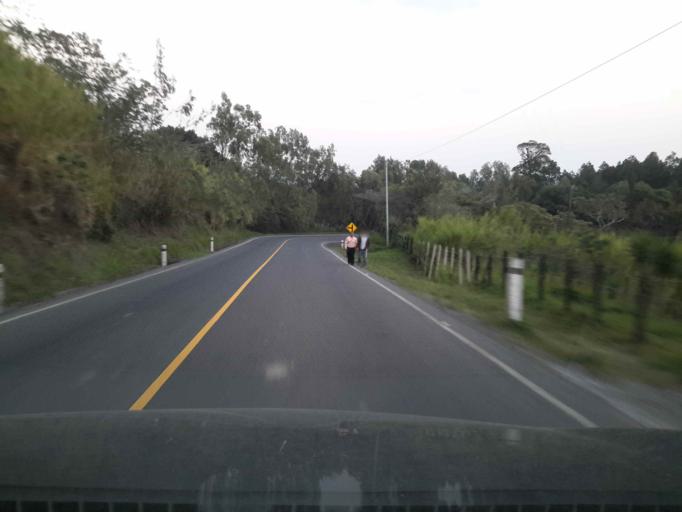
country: NI
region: Matagalpa
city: Matagalpa
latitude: 12.9985
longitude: -85.9219
